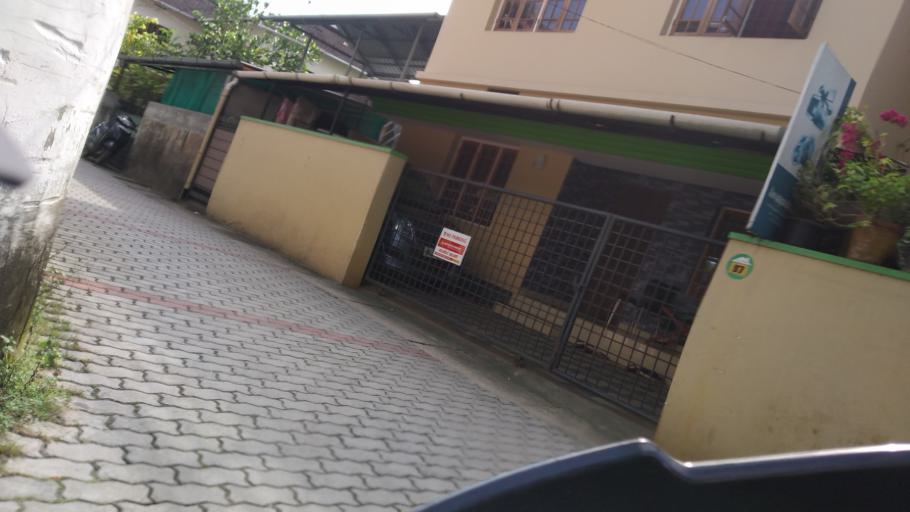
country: IN
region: Kerala
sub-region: Ernakulam
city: Cochin
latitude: 9.9874
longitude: 76.2993
